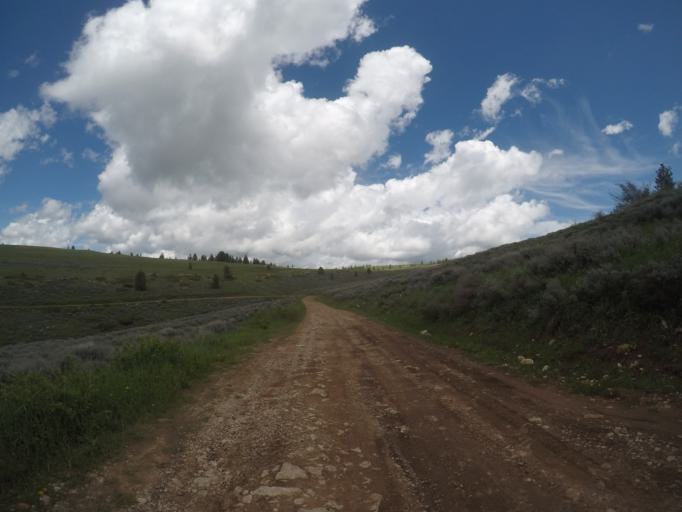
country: US
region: Wyoming
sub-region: Big Horn County
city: Lovell
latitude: 45.1801
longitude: -108.4367
